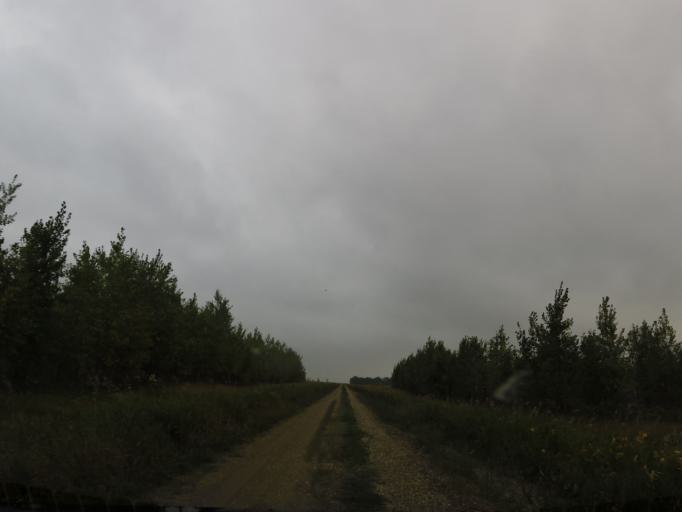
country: US
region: North Dakota
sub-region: Walsh County
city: Grafton
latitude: 48.4261
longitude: -97.1182
